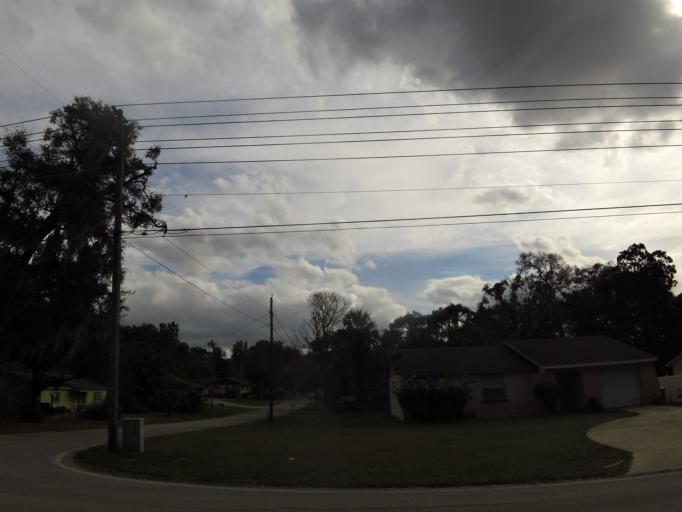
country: US
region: Florida
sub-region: Volusia County
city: Orange City
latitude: 28.9487
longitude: -81.2896
